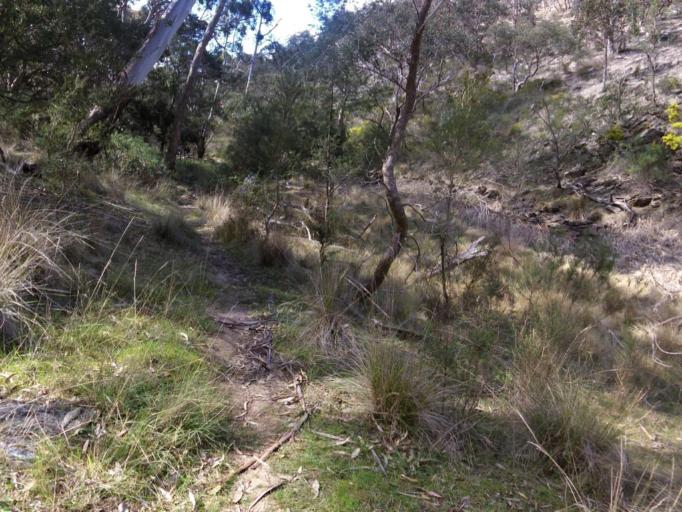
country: AU
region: Victoria
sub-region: Moorabool
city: Bacchus Marsh
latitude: -37.6599
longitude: 144.4970
